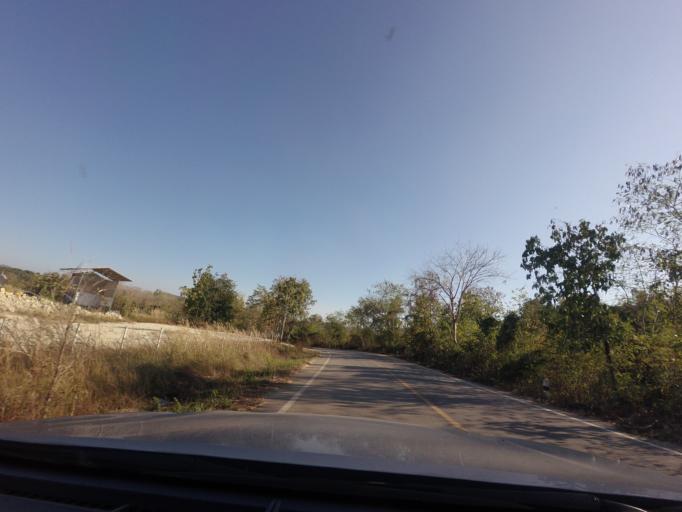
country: TH
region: Lampang
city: Chae Hom
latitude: 18.5314
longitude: 99.6428
